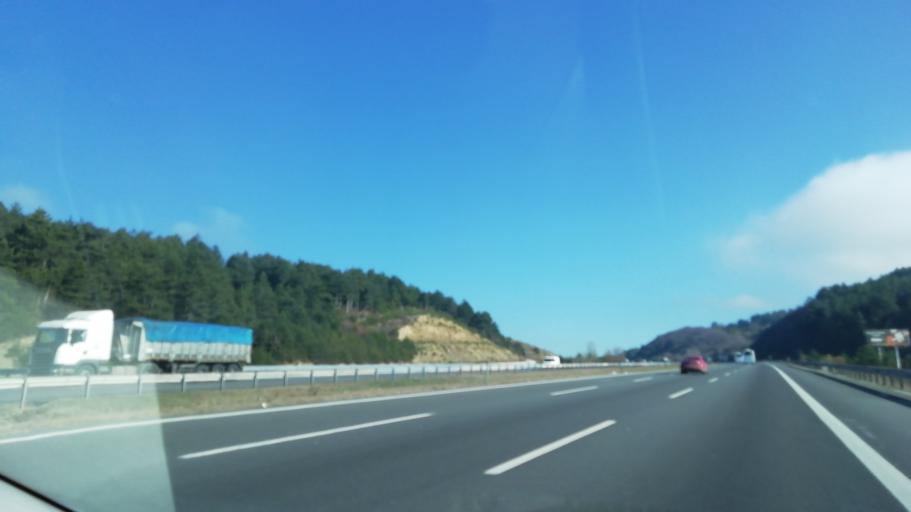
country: TR
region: Bolu
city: Yenicaga
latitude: 40.7482
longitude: 31.8901
